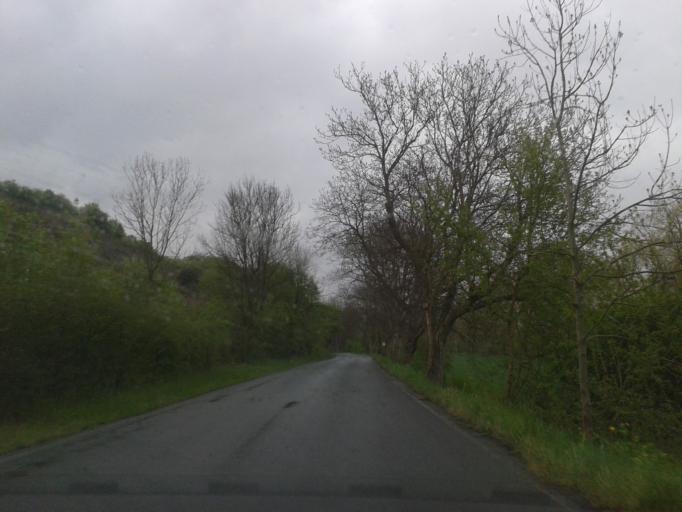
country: CZ
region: Central Bohemia
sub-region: Okres Beroun
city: Lodenice
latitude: 49.9312
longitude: 14.1504
